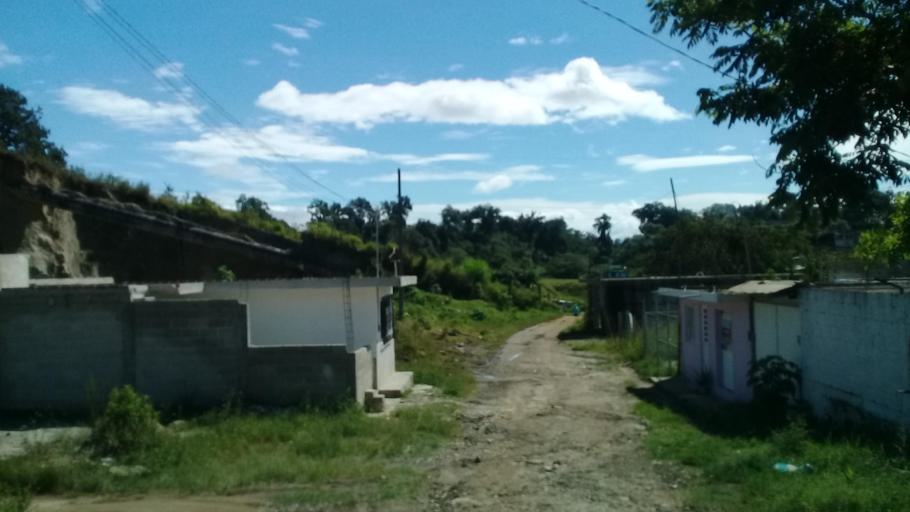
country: MX
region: Veracruz
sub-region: Jilotepec
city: El Pueblito (Garbanzal)
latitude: 19.5731
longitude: -96.8974
